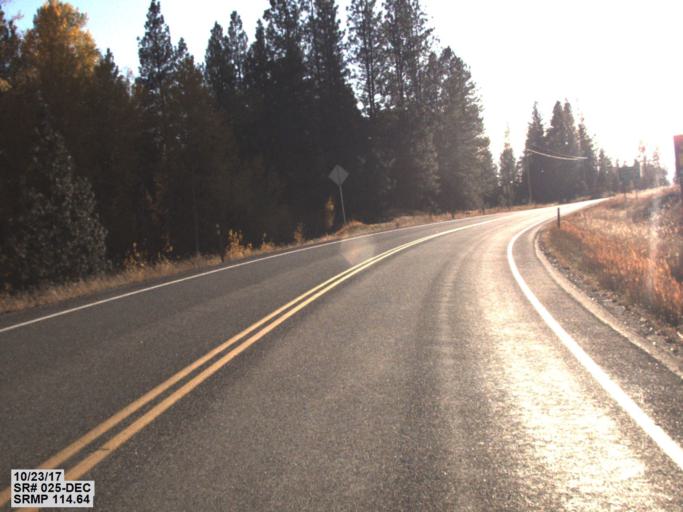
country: CA
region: British Columbia
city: Rossland
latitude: 48.9298
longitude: -117.7737
